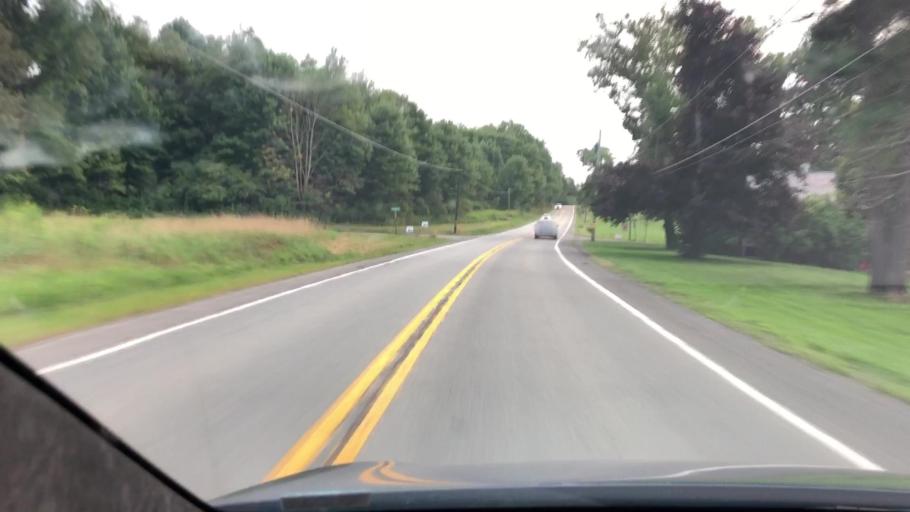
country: US
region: Pennsylvania
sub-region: Mercer County
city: Grove City
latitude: 41.1646
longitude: -79.9941
